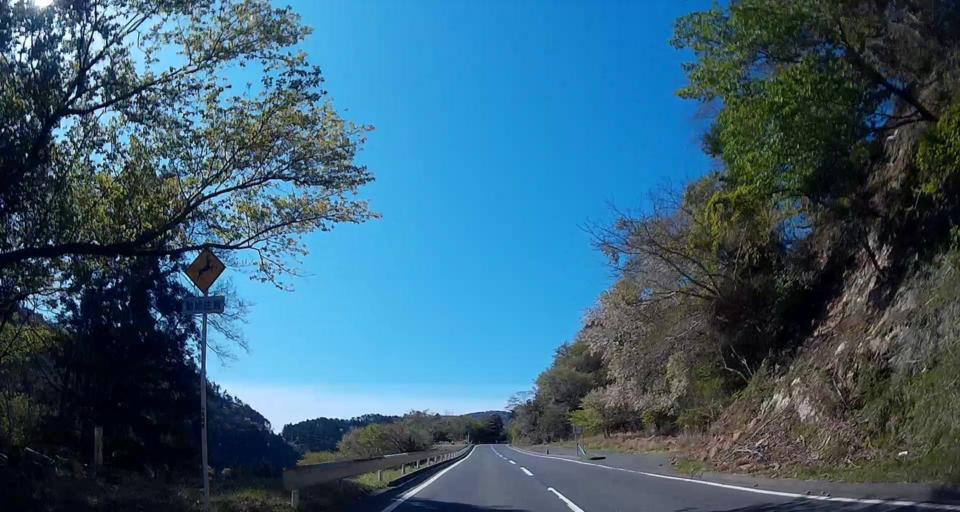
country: JP
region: Miyagi
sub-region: Oshika Gun
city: Onagawa Cho
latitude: 38.4316
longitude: 141.4476
